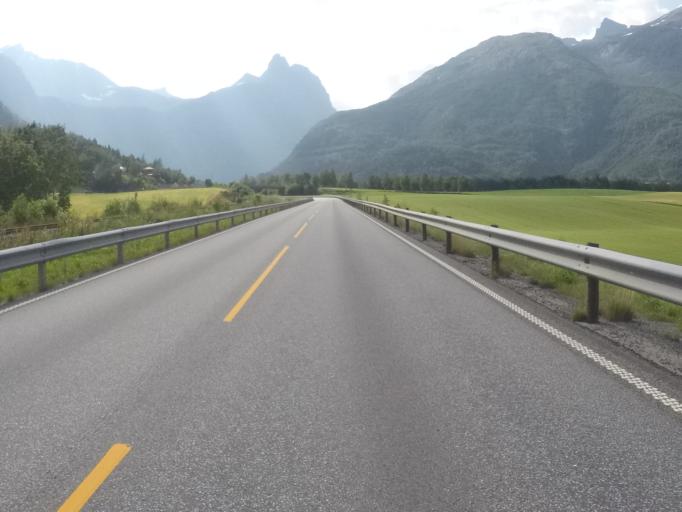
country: NO
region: More og Romsdal
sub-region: Rauma
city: Andalsnes
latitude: 62.5428
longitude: 7.7200
